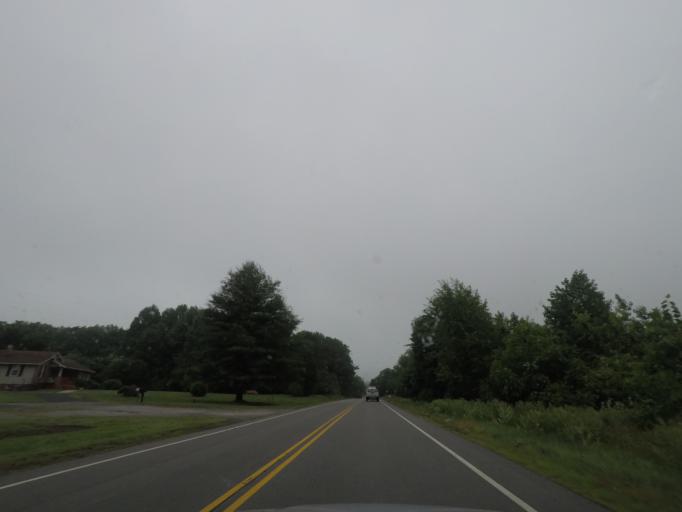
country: US
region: Virginia
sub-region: Buckingham County
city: Buckingham
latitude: 37.4472
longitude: -78.4561
